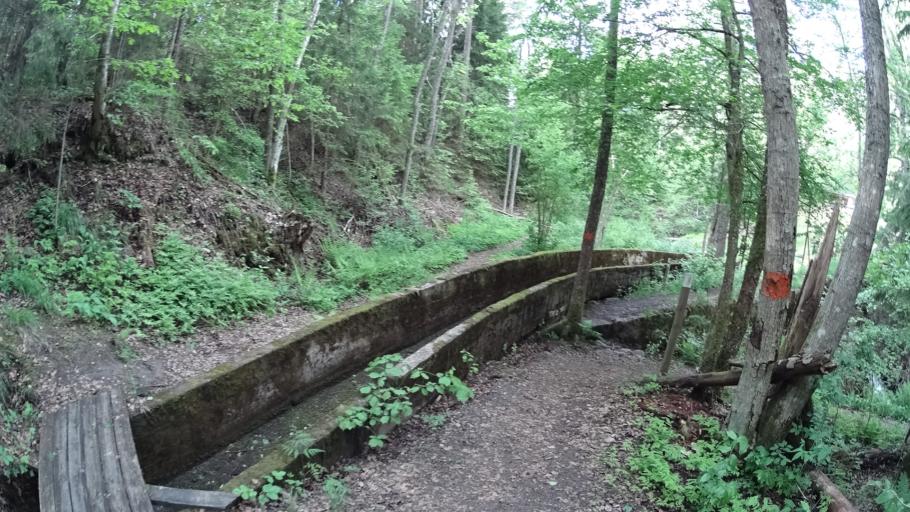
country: FI
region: Uusimaa
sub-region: Raaseporin
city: Pohja
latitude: 60.1456
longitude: 23.5405
